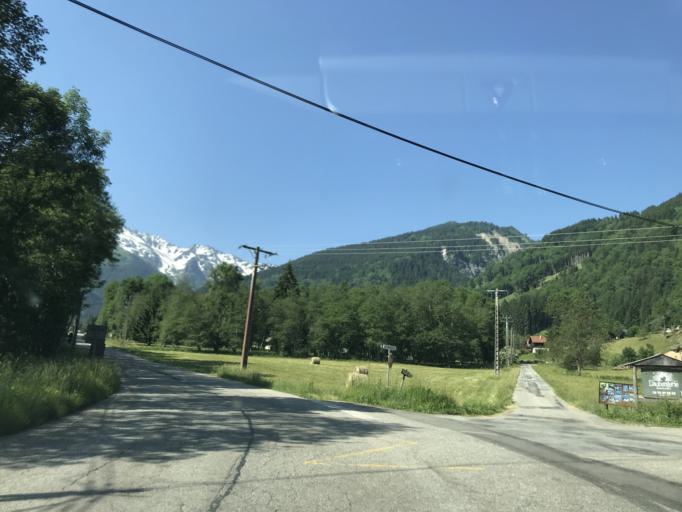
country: FR
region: Rhone-Alpes
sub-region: Departement de l'Isere
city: Theys
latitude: 45.2969
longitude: 6.0789
